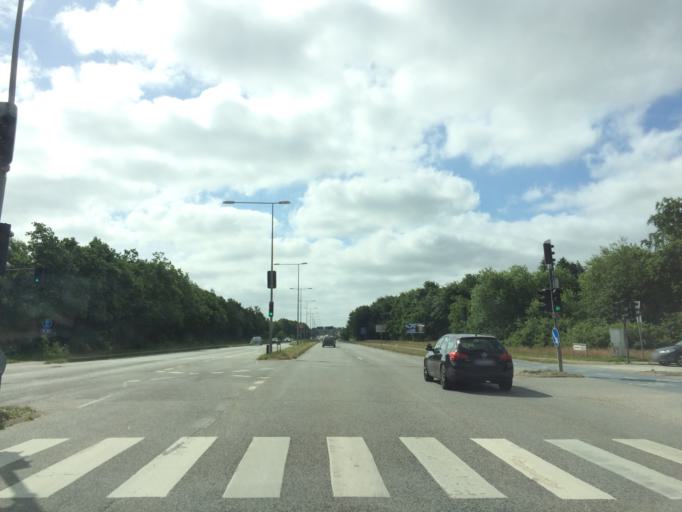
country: DK
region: Central Jutland
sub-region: Herning Kommune
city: Herning
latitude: 56.1454
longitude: 8.9391
